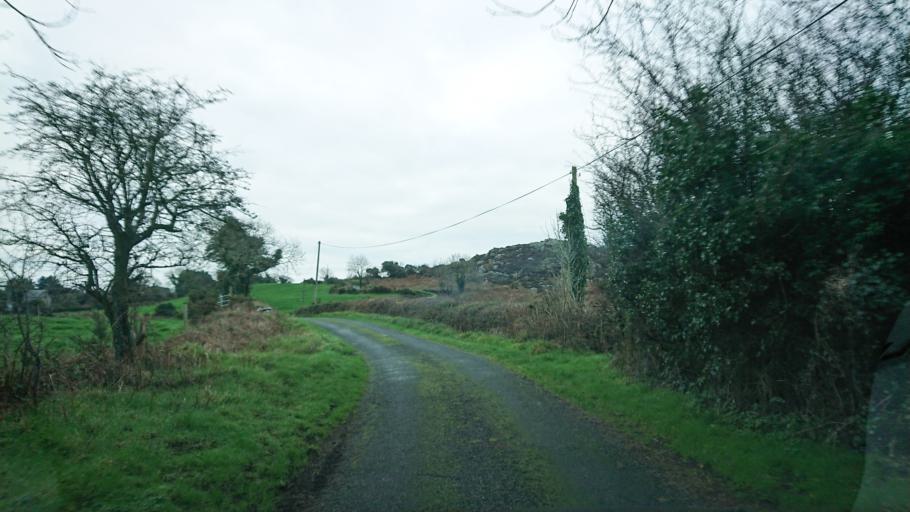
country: IE
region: Leinster
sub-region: Kilkenny
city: Mooncoin
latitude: 52.2113
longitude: -7.2702
